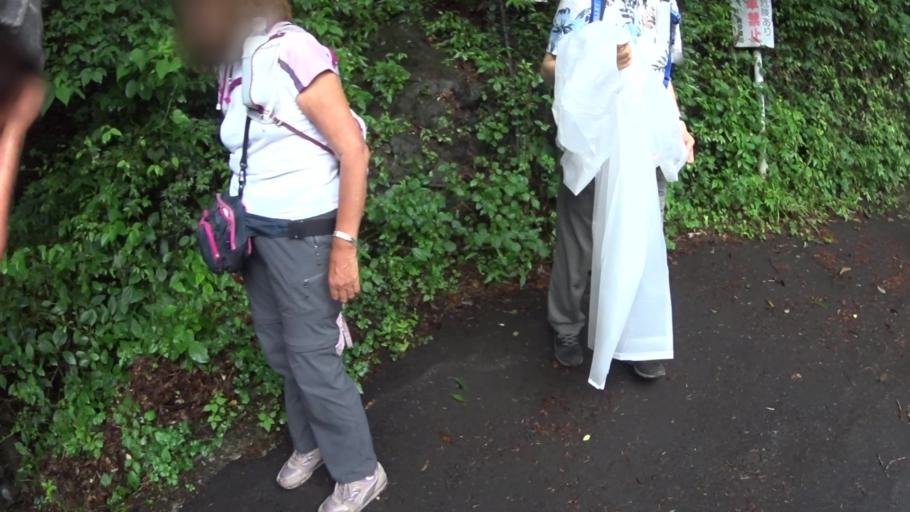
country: JP
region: Tokyo
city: Itsukaichi
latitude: 35.7936
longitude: 139.0674
